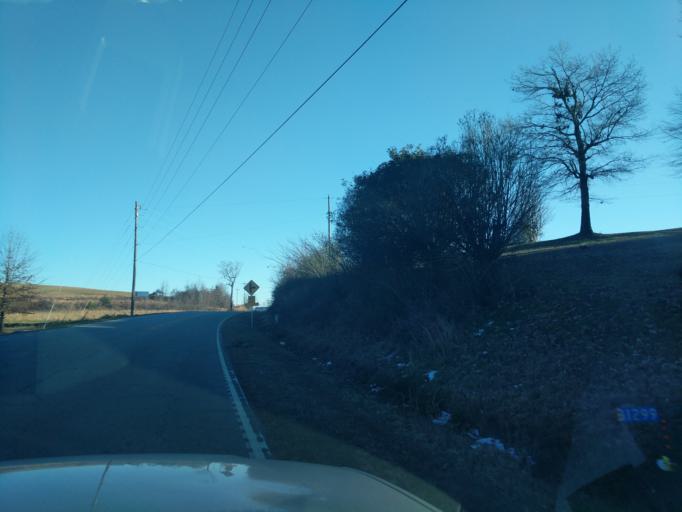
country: US
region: South Carolina
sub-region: Oconee County
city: Westminster
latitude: 34.7182
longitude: -83.2061
